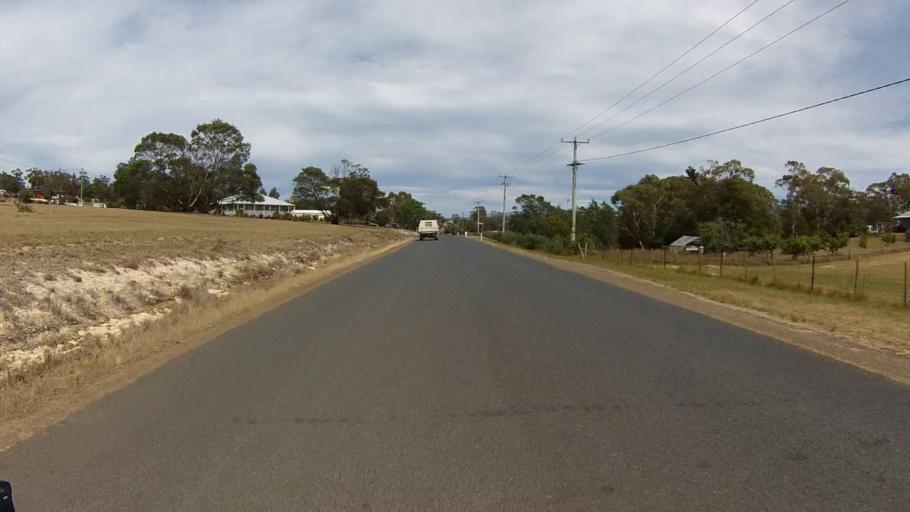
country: AU
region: Tasmania
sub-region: Sorell
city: Sorell
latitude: -42.8053
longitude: 147.6401
